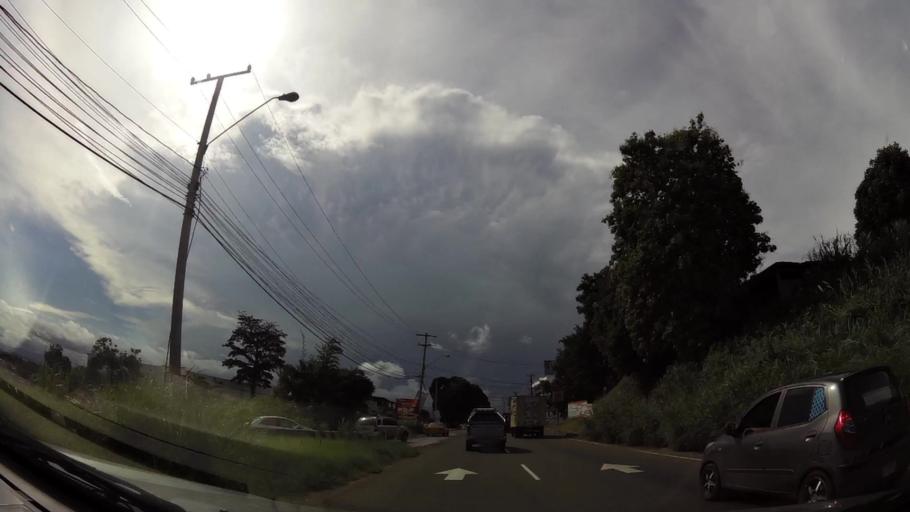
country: PA
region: Panama
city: La Chorrera
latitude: 8.8892
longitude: -79.7686
